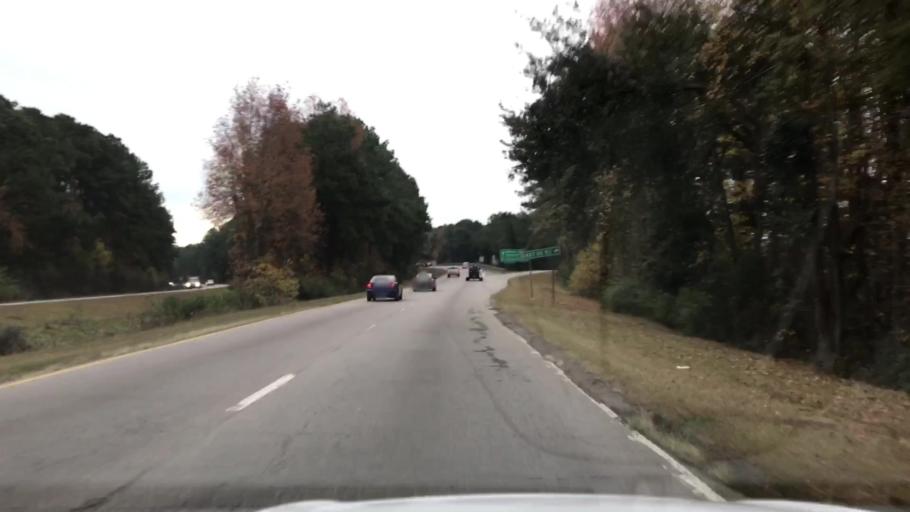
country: US
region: South Carolina
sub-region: Berkeley County
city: Hanahan
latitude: 32.9463
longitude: -80.0452
